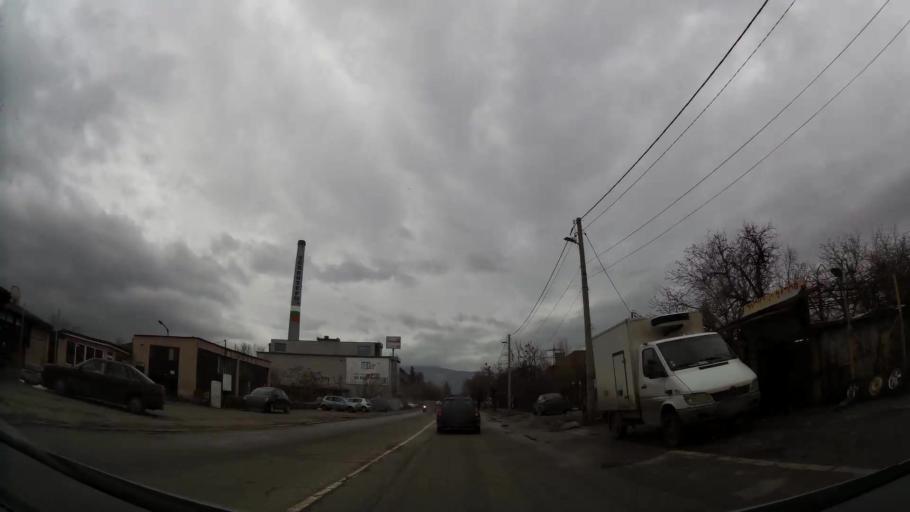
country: BG
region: Sofia-Capital
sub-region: Stolichna Obshtina
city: Sofia
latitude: 42.7243
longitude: 23.2813
